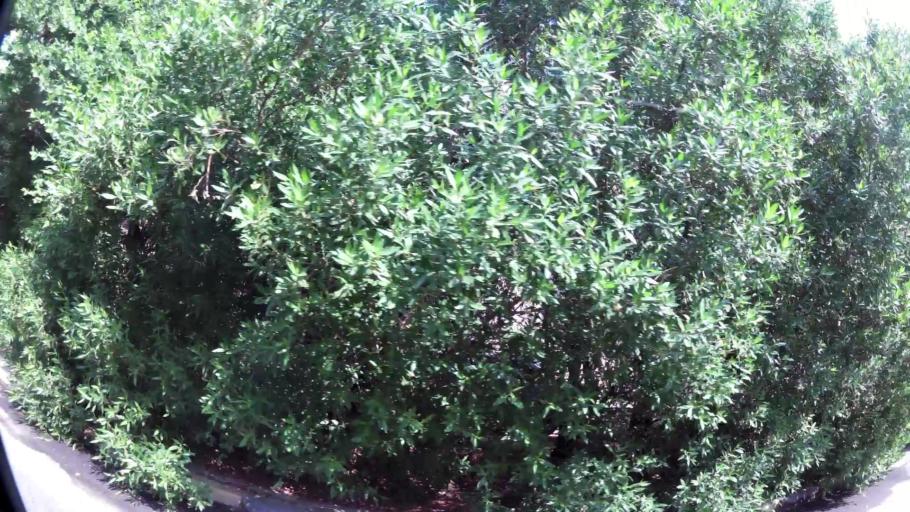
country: KW
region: Muhafazat al Jahra'
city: Al Jahra'
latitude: 29.3194
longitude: 47.6714
